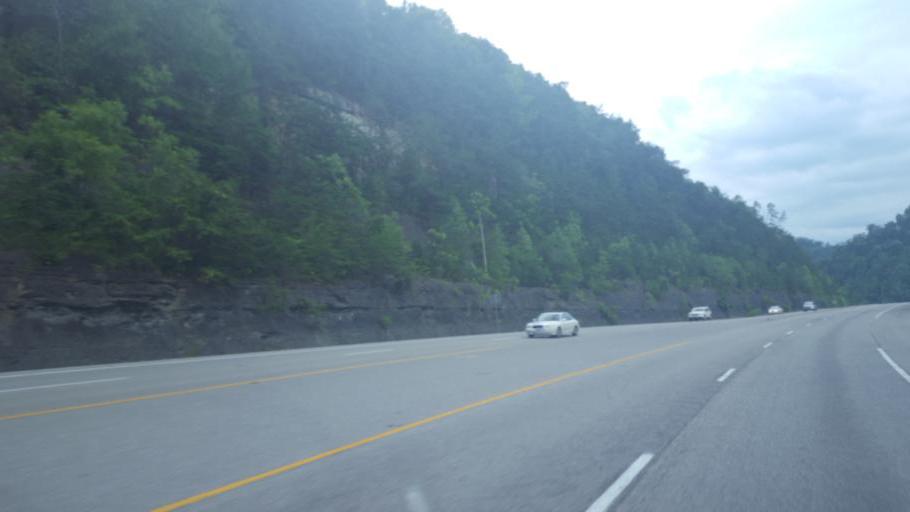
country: US
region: Kentucky
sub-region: Pike County
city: Pikeville
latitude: 37.3670
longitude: -82.5490
